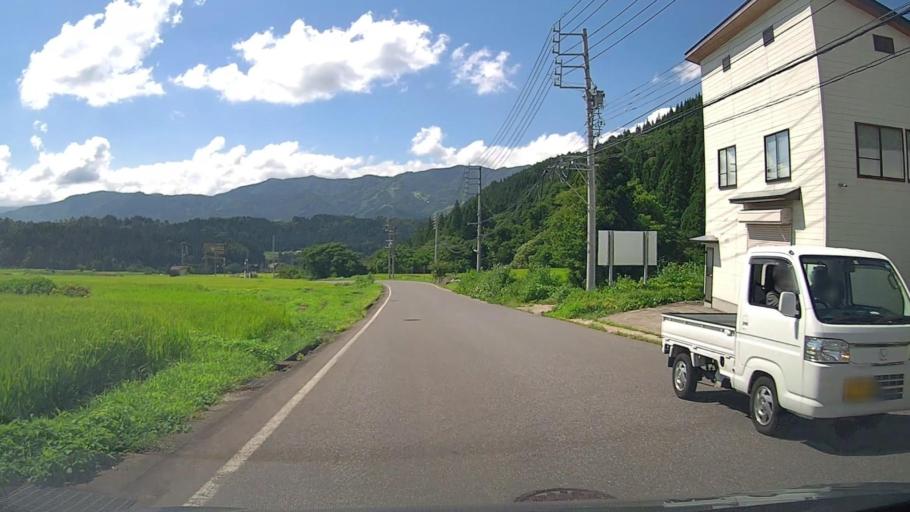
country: JP
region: Nagano
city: Iiyama
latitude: 36.9223
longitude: 138.4372
